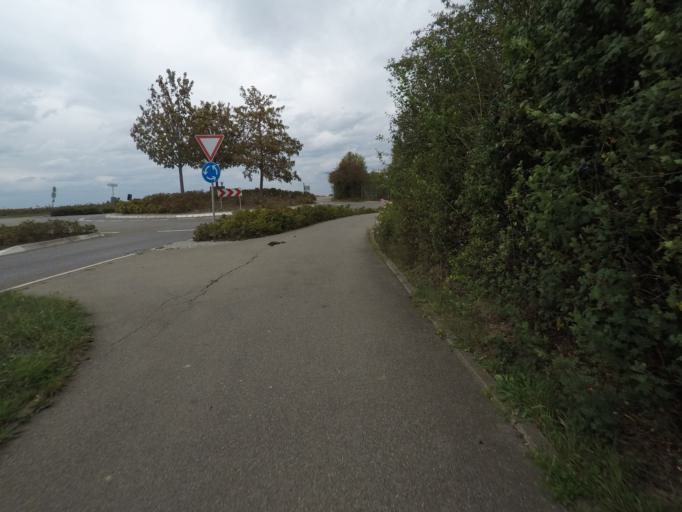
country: DE
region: Baden-Wuerttemberg
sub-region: Regierungsbezirk Stuttgart
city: Filderstadt
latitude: 48.6456
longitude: 9.2301
